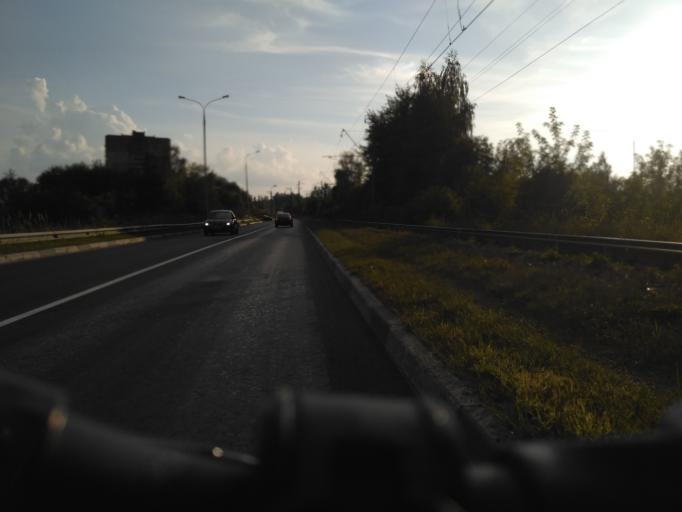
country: RU
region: Moskovskaya
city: Dubna
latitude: 56.7375
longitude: 37.1549
